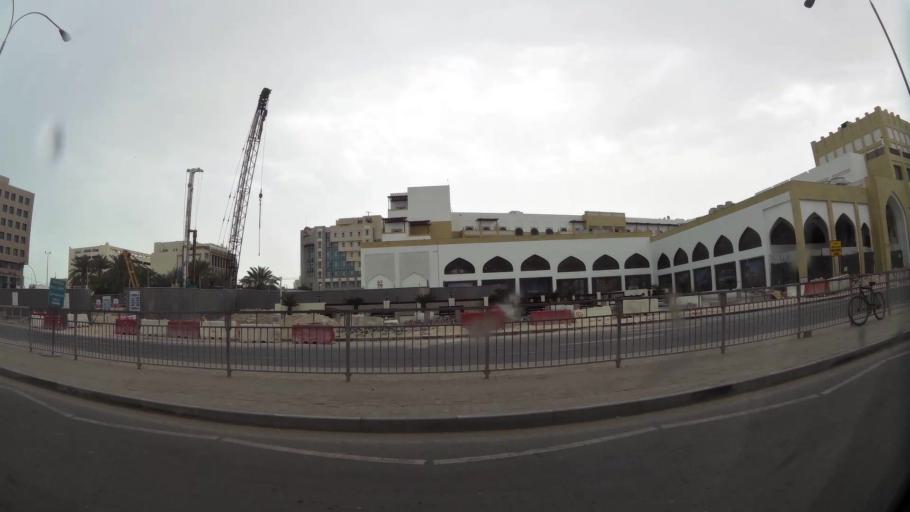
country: QA
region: Baladiyat ad Dawhah
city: Doha
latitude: 25.2862
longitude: 51.5338
